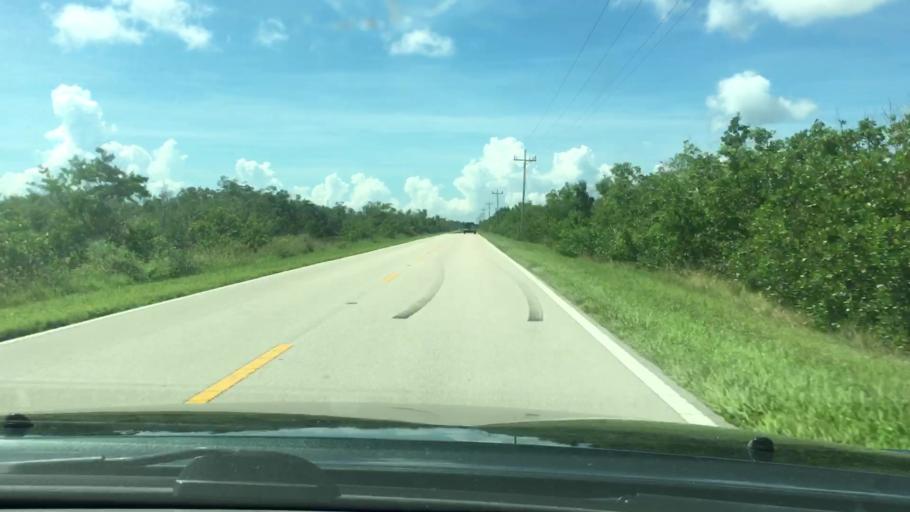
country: US
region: Florida
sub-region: Collier County
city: Marco
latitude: 25.9479
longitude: -81.6428
